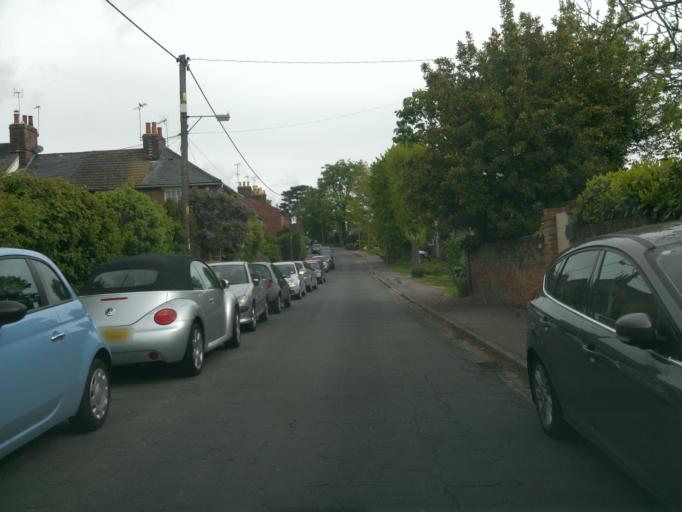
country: GB
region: England
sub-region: Essex
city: Wivenhoe
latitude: 51.8572
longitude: 0.9610
